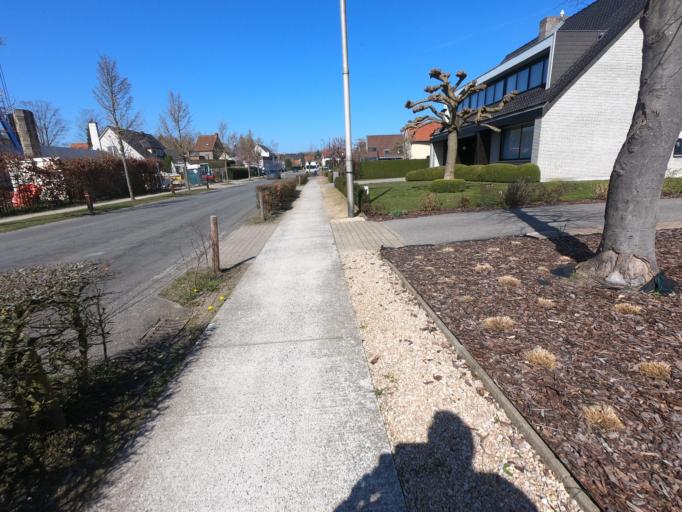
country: BE
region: Flanders
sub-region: Provincie Oost-Vlaanderen
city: Sint-Martens-Latem
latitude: 51.0081
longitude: 3.6344
